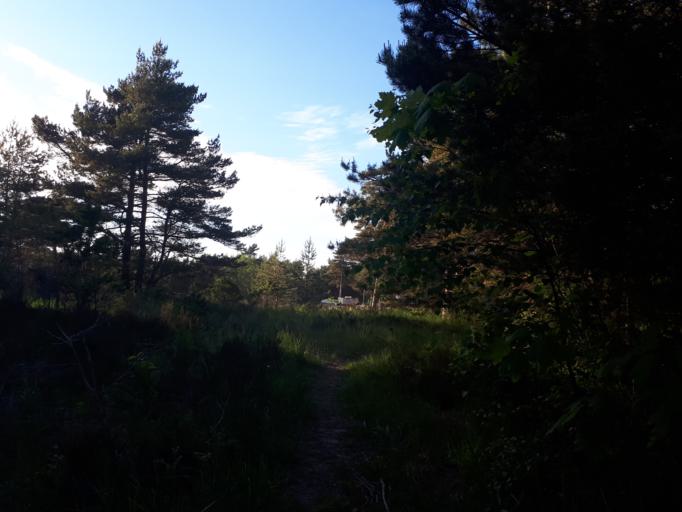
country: SE
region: Gotland
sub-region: Gotland
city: Visby
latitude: 57.6053
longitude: 18.2894
